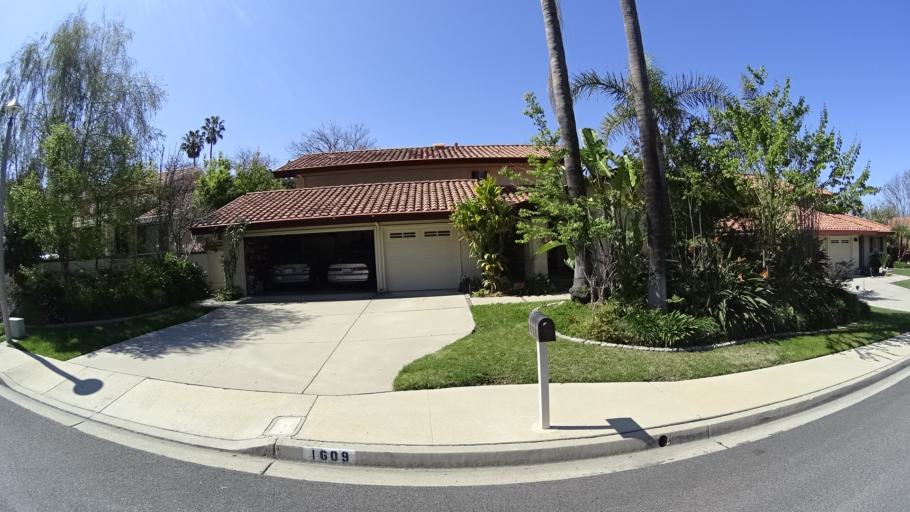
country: US
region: California
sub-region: Ventura County
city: Thousand Oaks
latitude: 34.2314
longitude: -118.8501
